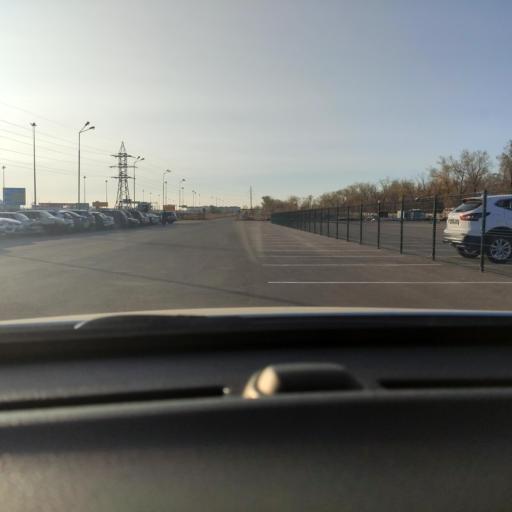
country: RU
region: Voronezj
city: Somovo
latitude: 51.6616
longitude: 39.3007
